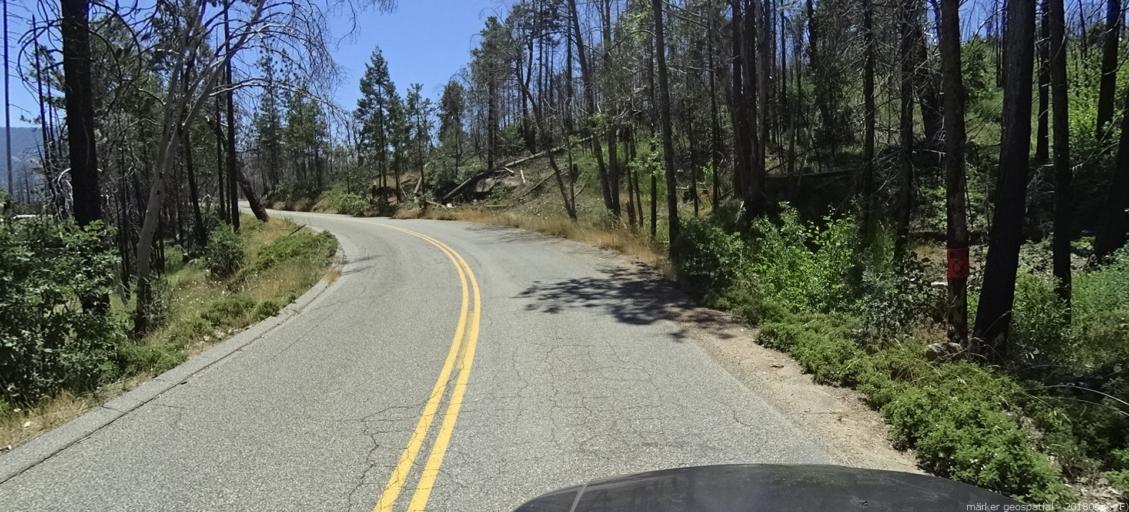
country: US
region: California
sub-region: Fresno County
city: Auberry
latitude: 37.2704
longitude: -119.3597
